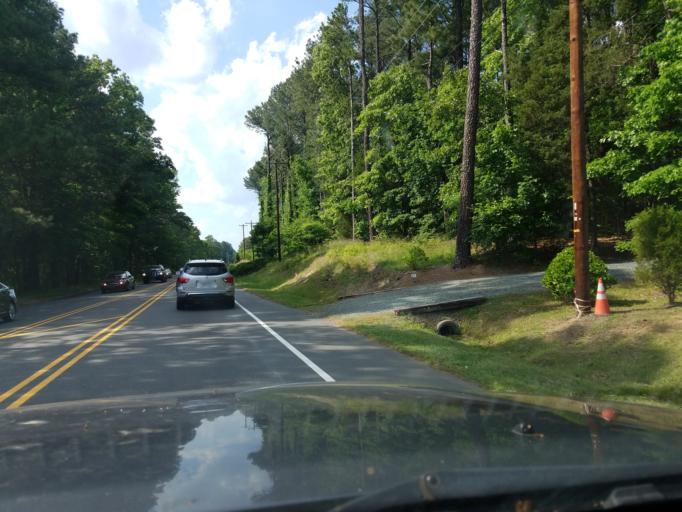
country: US
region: North Carolina
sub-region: Durham County
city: Durham
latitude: 35.9369
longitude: -78.9630
